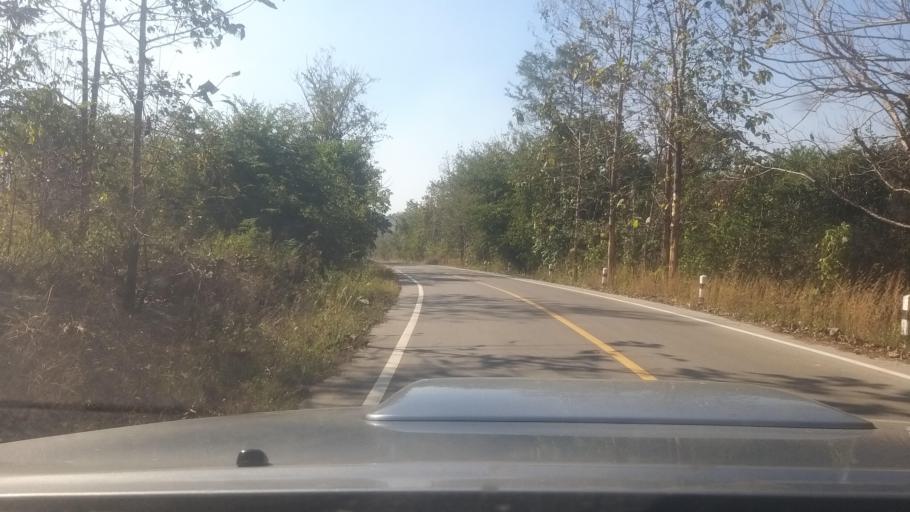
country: TH
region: Phrae
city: Nong Muang Khai
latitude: 18.2968
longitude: 100.0497
